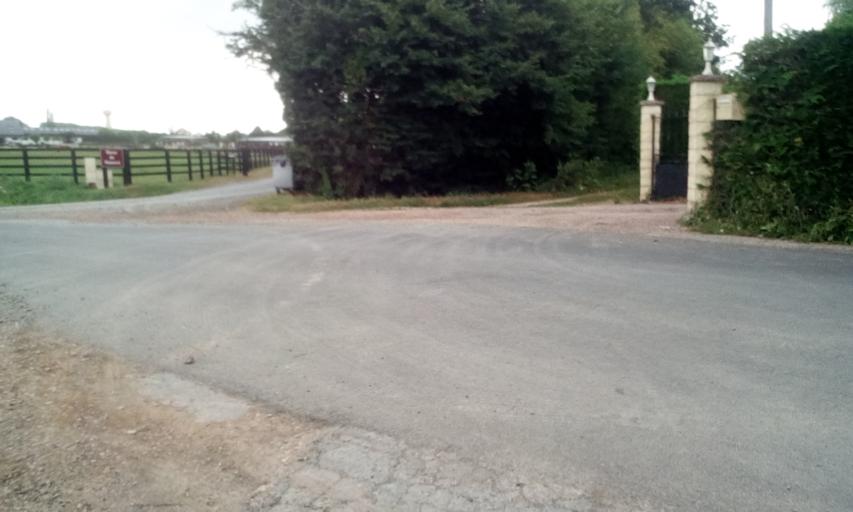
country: FR
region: Lower Normandy
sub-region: Departement du Calvados
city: Sannerville
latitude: 49.1860
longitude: -0.2152
